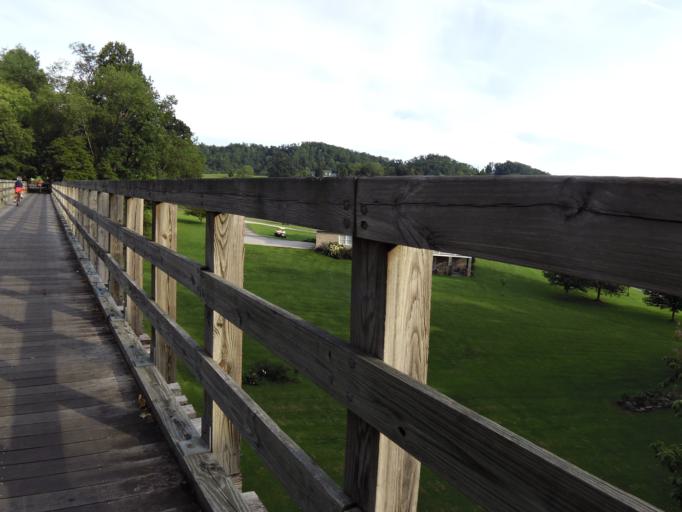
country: US
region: Virginia
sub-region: Washington County
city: Abingdon
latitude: 36.6786
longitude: -81.9364
